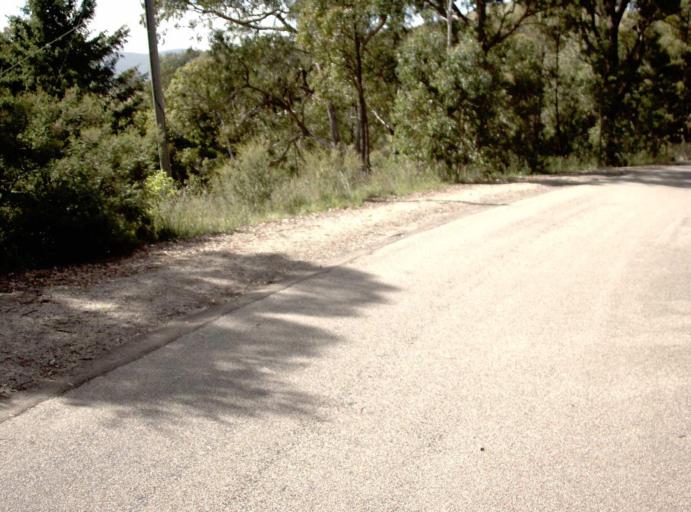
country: AU
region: Victoria
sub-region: East Gippsland
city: Lakes Entrance
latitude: -37.5086
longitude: 148.1387
